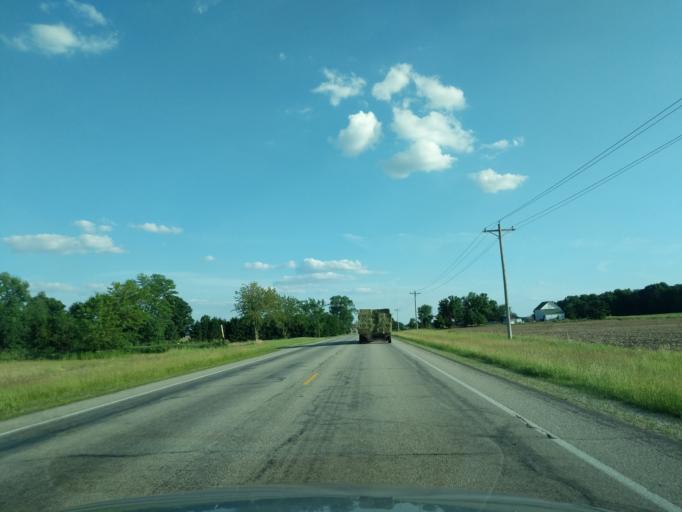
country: US
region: Indiana
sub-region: Huntington County
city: Roanoke
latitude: 41.0307
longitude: -85.4707
